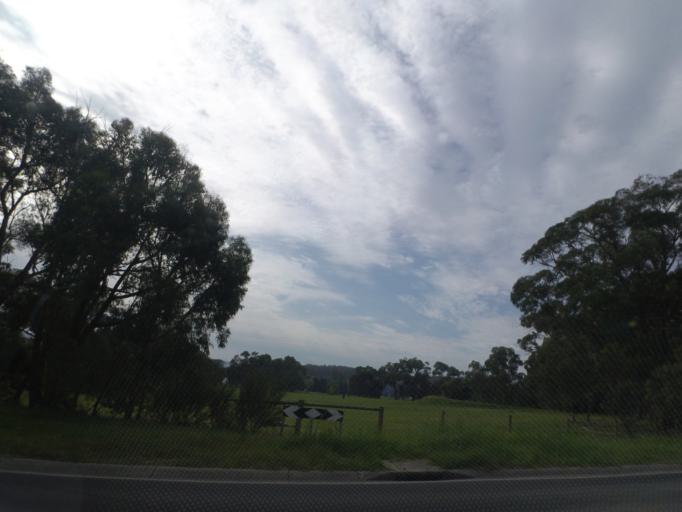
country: AU
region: Victoria
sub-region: Maroondah
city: Kilsyth South
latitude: -37.8315
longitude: 145.3336
